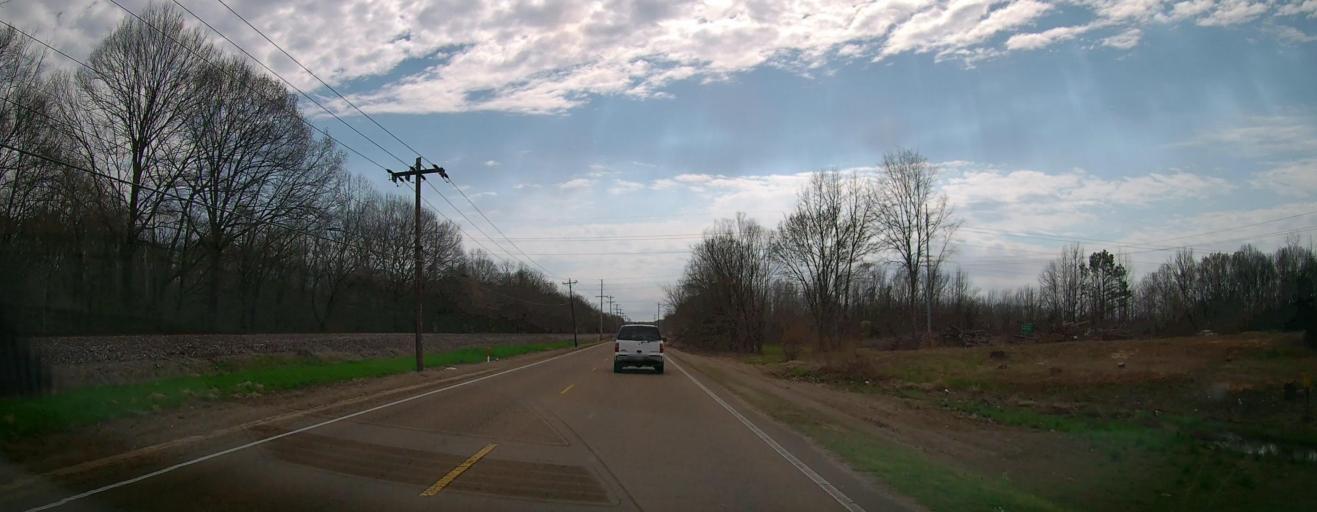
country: US
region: Mississippi
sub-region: Marshall County
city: Byhalia
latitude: 34.9125
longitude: -89.7610
